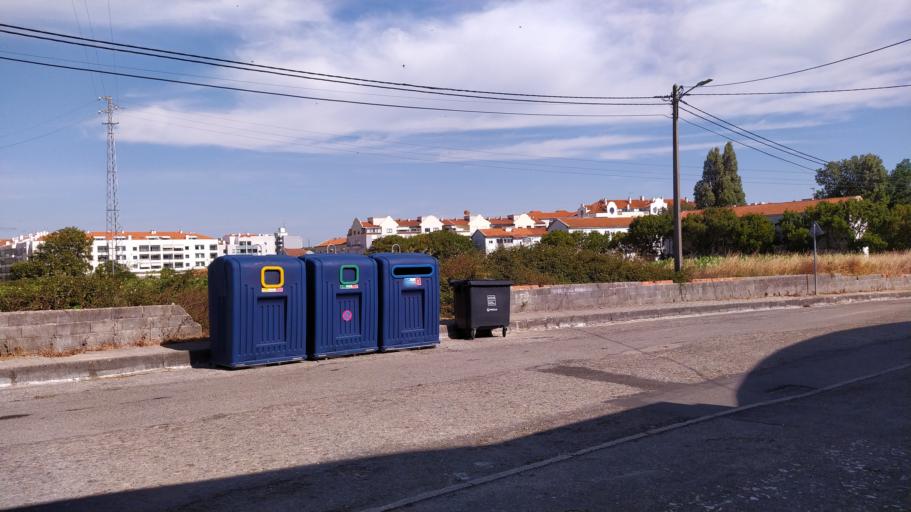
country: PT
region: Aveiro
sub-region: Aveiro
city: Aveiro
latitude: 40.6488
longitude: -8.6418
